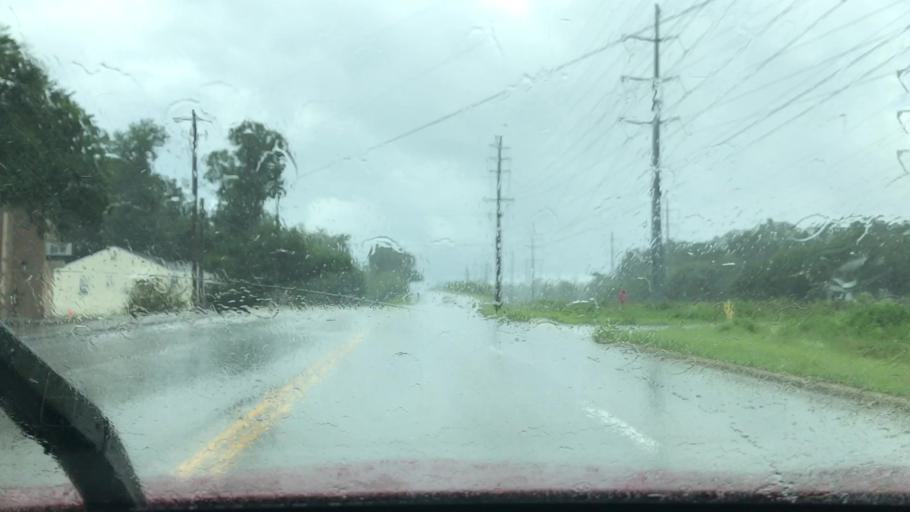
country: US
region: South Carolina
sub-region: Charleston County
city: North Charleston
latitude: 32.8474
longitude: -79.9831
